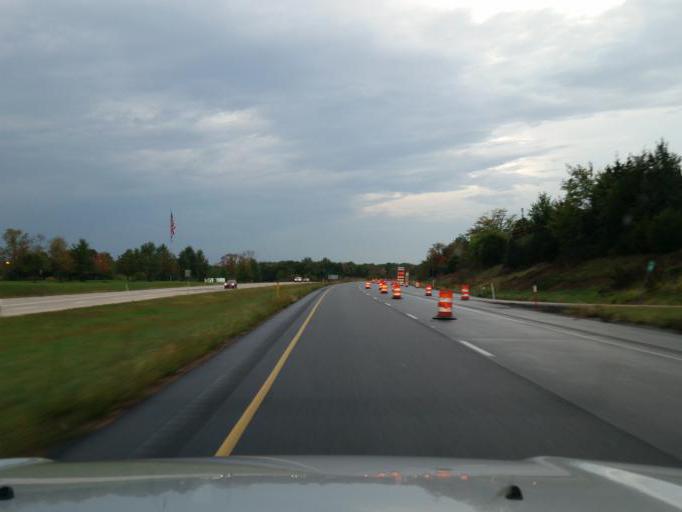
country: US
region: Pennsylvania
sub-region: Adams County
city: Lake Heritage
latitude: 39.7979
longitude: -77.2019
